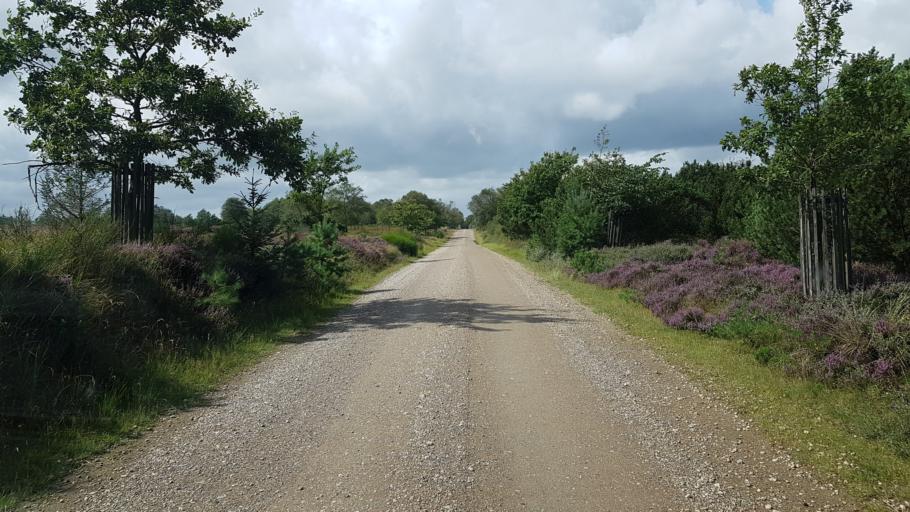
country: DK
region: South Denmark
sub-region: Vejen Kommune
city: Holsted
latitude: 55.5958
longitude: 8.8807
